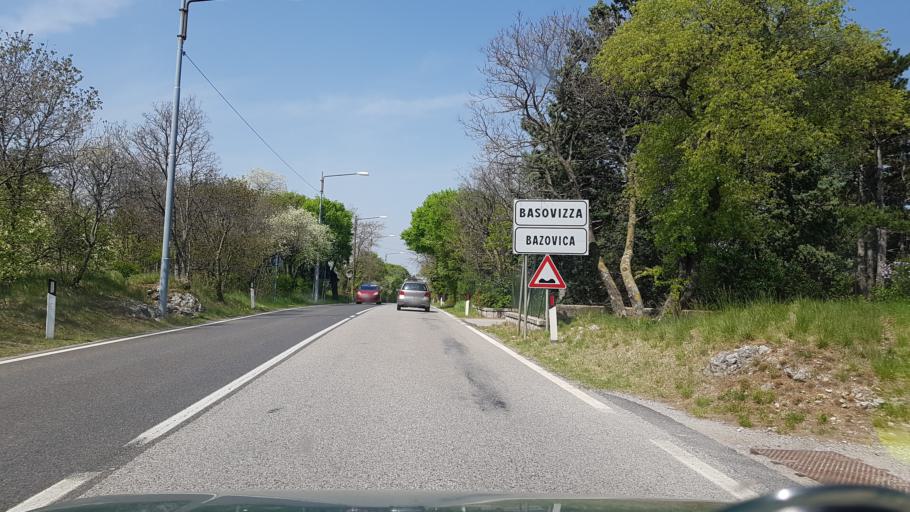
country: IT
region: Friuli Venezia Giulia
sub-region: Provincia di Trieste
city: Dolina
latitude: 45.6389
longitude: 13.8677
